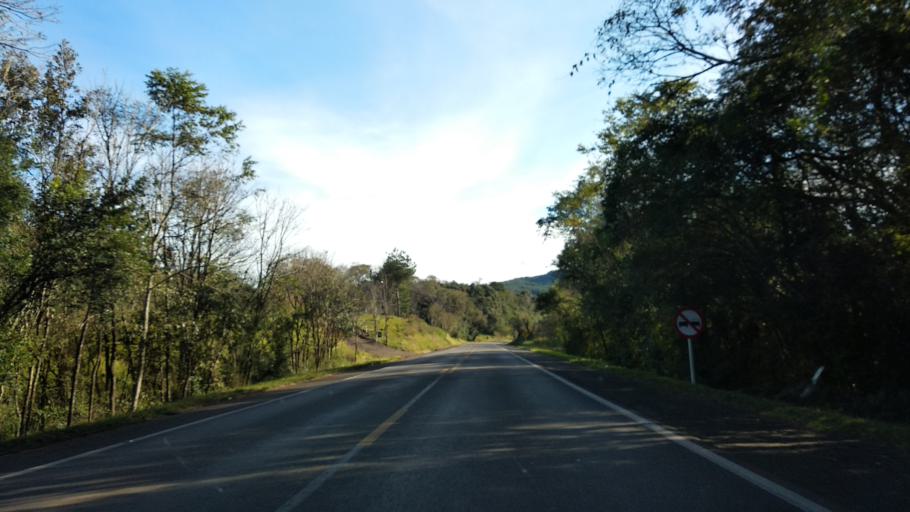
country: BR
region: Santa Catarina
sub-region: Celso Ramos
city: Celso Ramos
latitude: -27.5482
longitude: -51.4352
